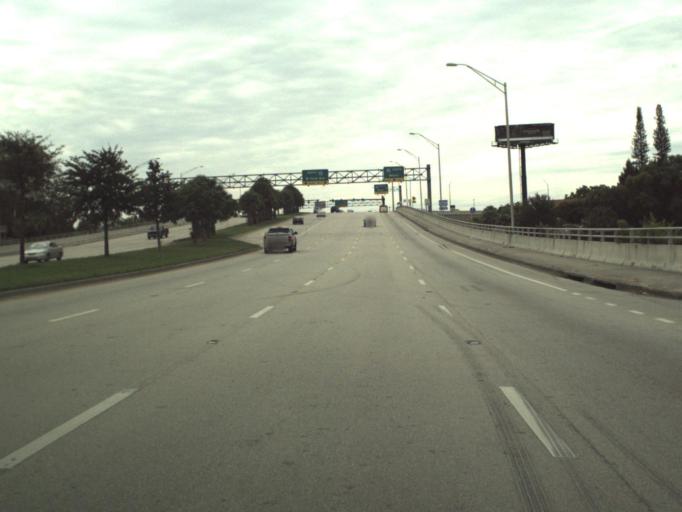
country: US
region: Florida
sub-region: Palm Beach County
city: Lake Clarke Shores
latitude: 26.6762
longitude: -80.0742
